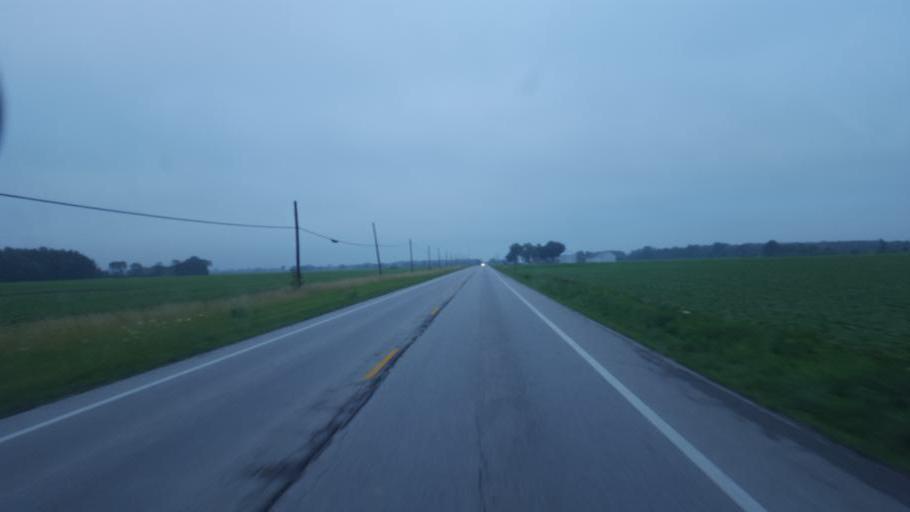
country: US
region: Ohio
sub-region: Madison County
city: Mount Sterling
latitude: 39.7067
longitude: -83.2771
